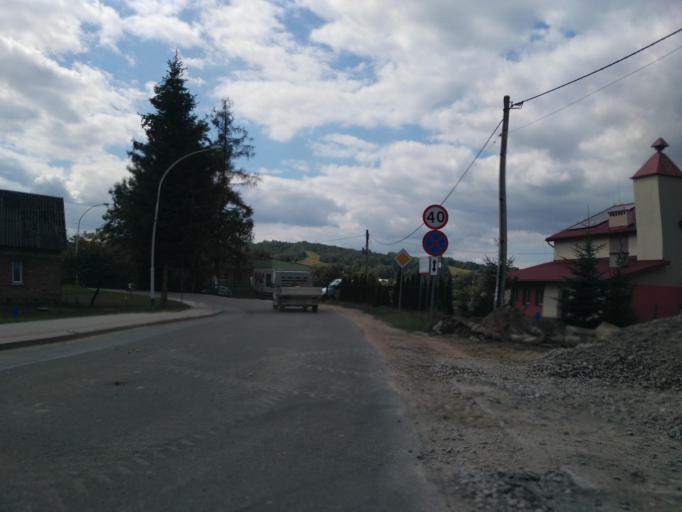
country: PL
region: Subcarpathian Voivodeship
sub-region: Powiat rzeszowski
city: Dynow
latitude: 49.8055
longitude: 22.2481
